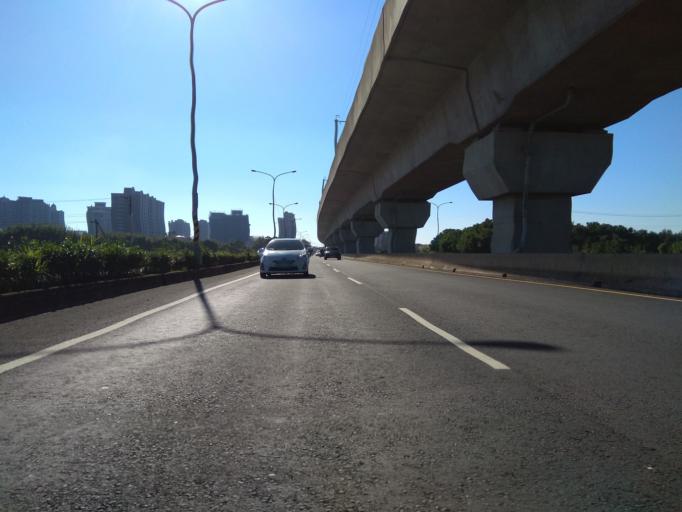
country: TW
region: Taiwan
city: Taoyuan City
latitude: 24.9666
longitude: 121.1687
